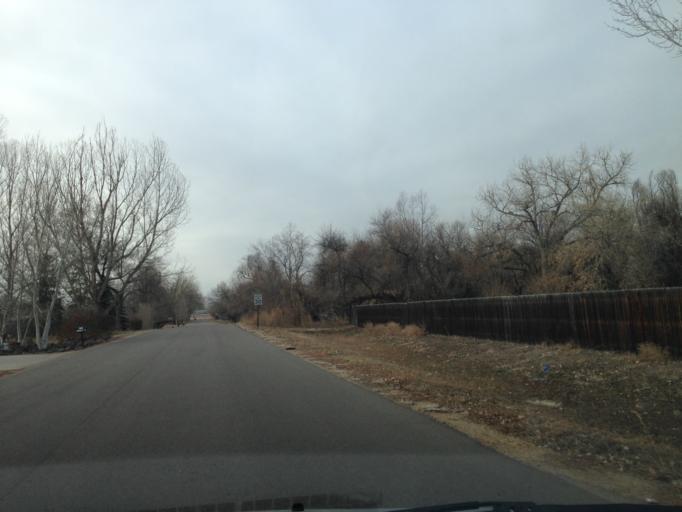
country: US
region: Colorado
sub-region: Boulder County
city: Erie
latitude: 40.0447
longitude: -105.0924
